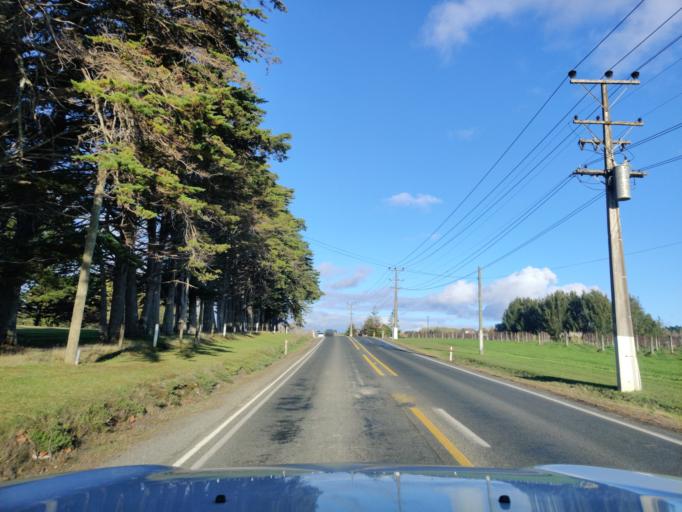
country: NZ
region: Auckland
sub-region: Auckland
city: Pakuranga
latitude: -36.9568
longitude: 174.9703
